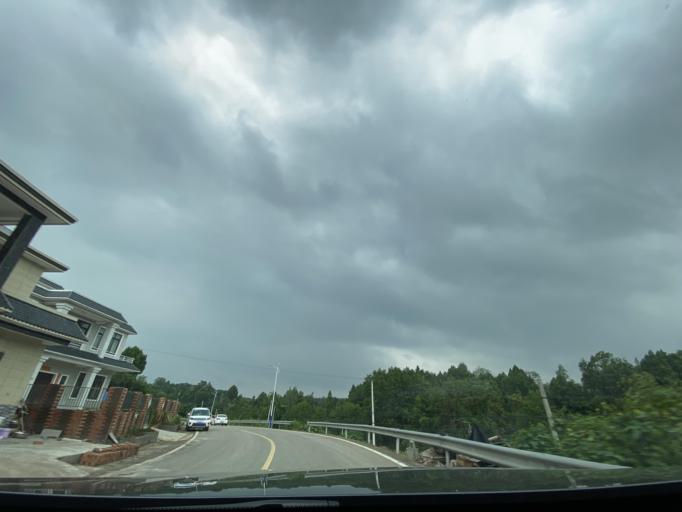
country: CN
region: Sichuan
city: Jiancheng
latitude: 30.5480
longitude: 104.5227
